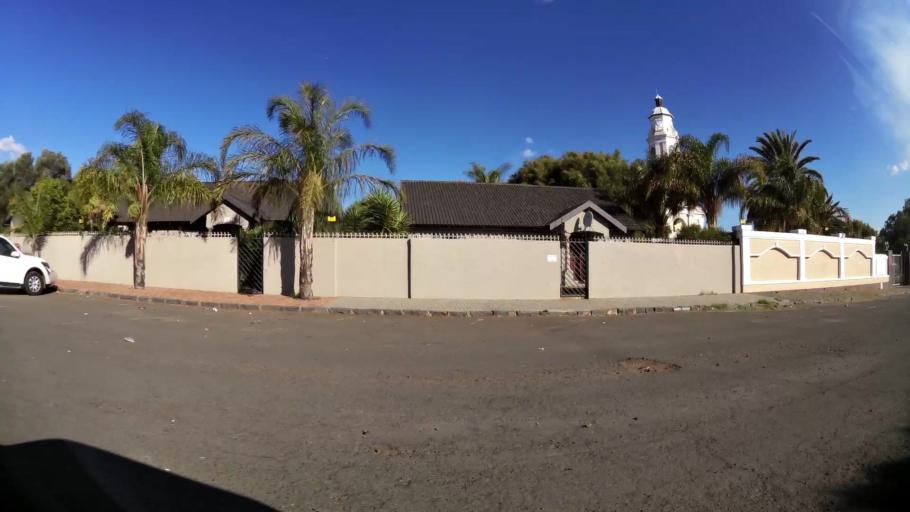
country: ZA
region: Northern Cape
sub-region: Frances Baard District Municipality
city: Kimberley
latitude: -28.7444
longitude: 24.7590
